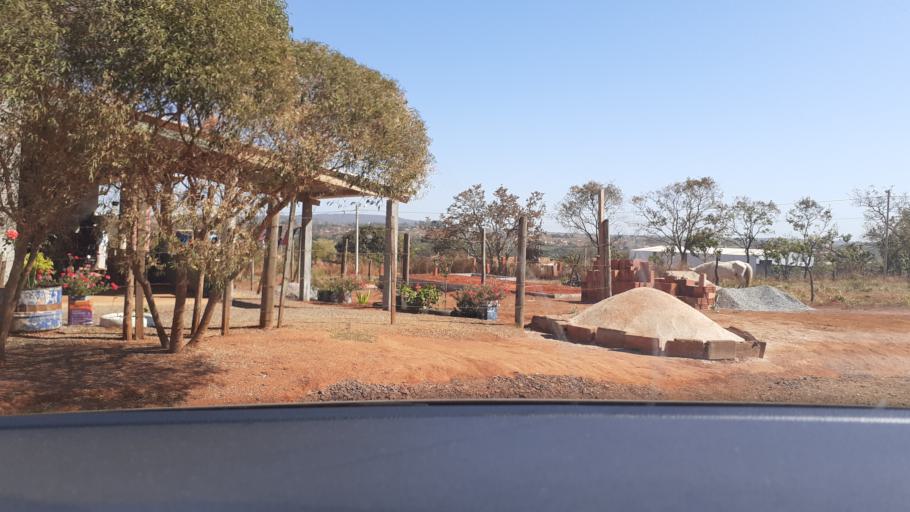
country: BR
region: Goias
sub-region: Aparecida De Goiania
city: Aparecida de Goiania
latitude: -16.8897
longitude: -49.2579
